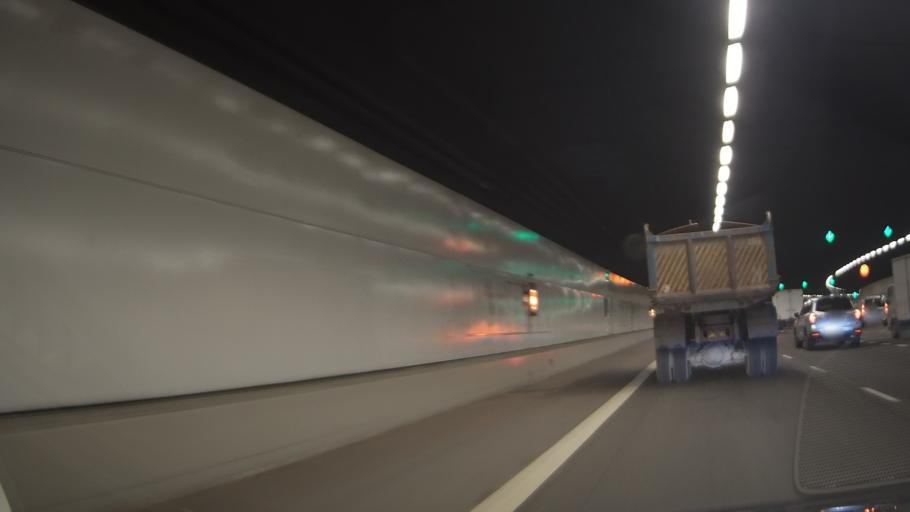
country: SG
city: Singapore
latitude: 1.2930
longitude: 103.8738
